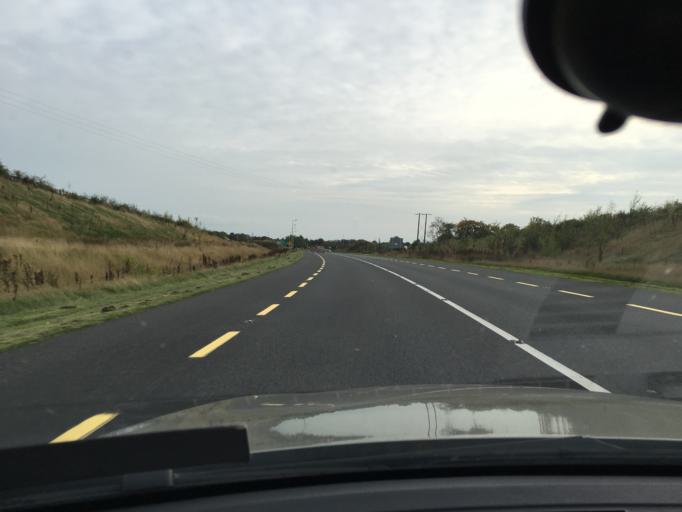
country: IE
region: Leinster
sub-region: An Longfort
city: Longford
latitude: 53.7282
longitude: -7.8255
